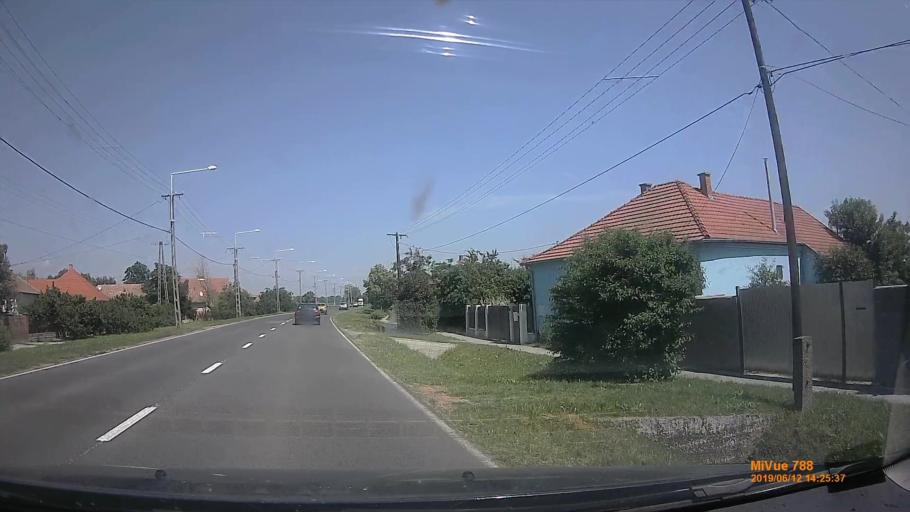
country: HU
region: Csongrad
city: Maroslele
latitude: 46.2195
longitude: 20.3293
